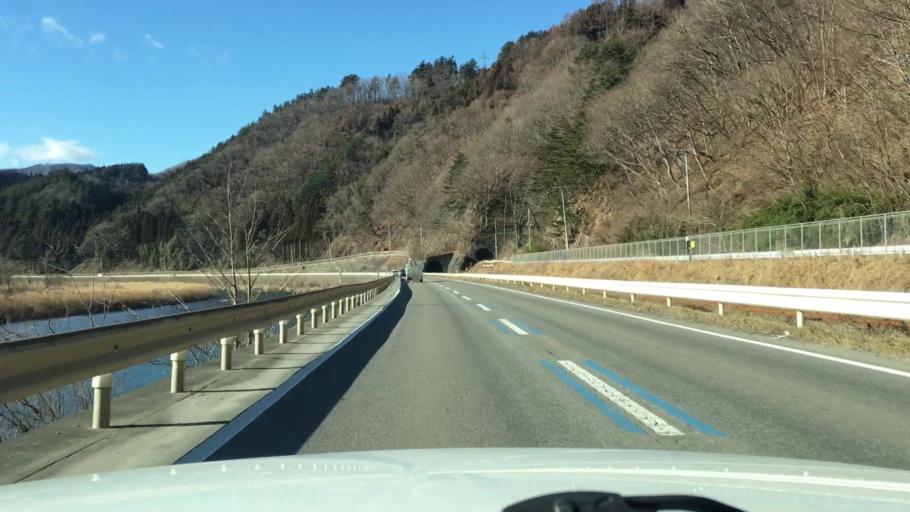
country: JP
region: Iwate
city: Miyako
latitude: 39.6344
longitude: 141.8496
